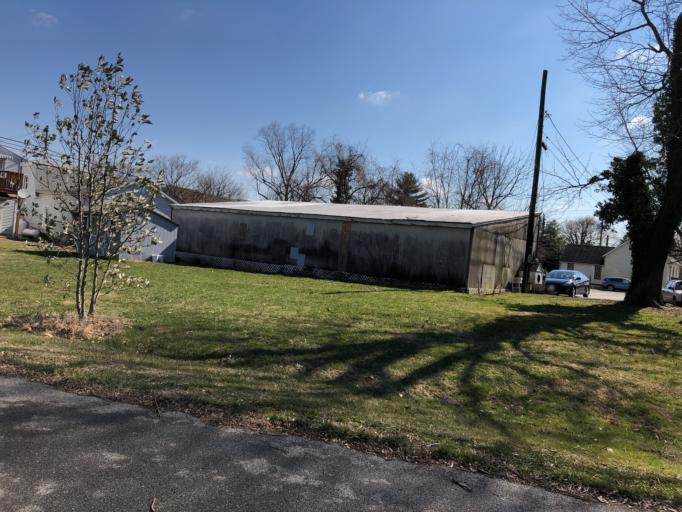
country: US
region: Maryland
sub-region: Kent County
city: Chestertown
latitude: 39.2135
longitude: -76.0742
